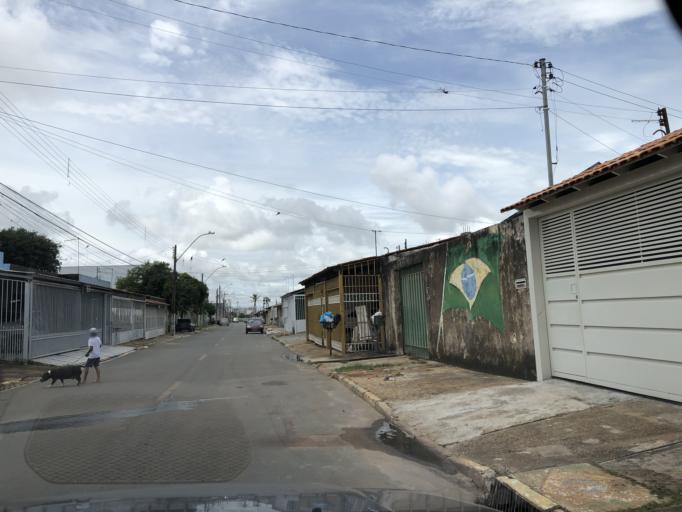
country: BR
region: Federal District
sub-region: Brasilia
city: Brasilia
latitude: -15.8161
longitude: -48.1198
